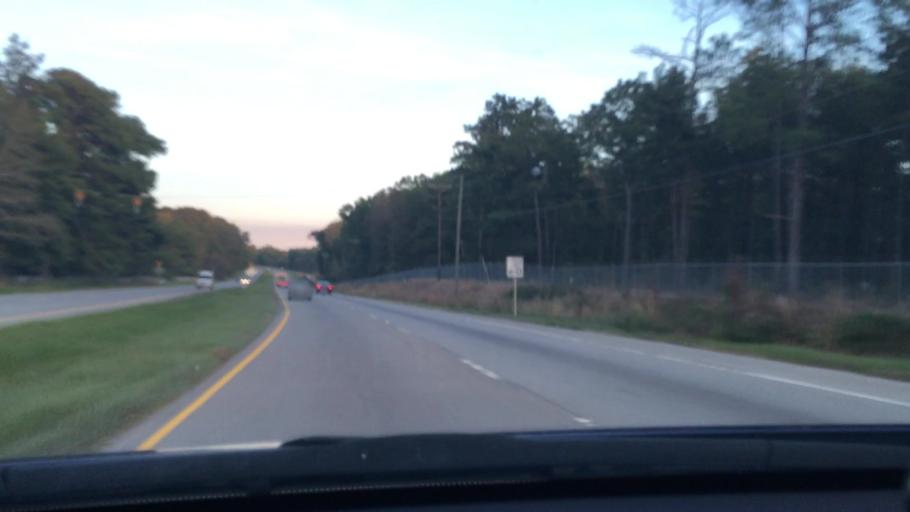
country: US
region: South Carolina
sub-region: Richland County
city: Hopkins
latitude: 33.9399
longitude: -80.7991
